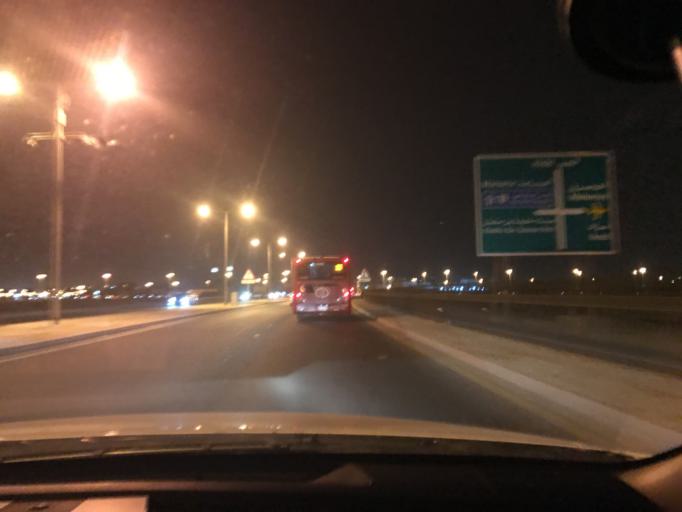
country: BH
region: Muharraq
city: Al Hadd
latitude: 26.2579
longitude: 50.6557
